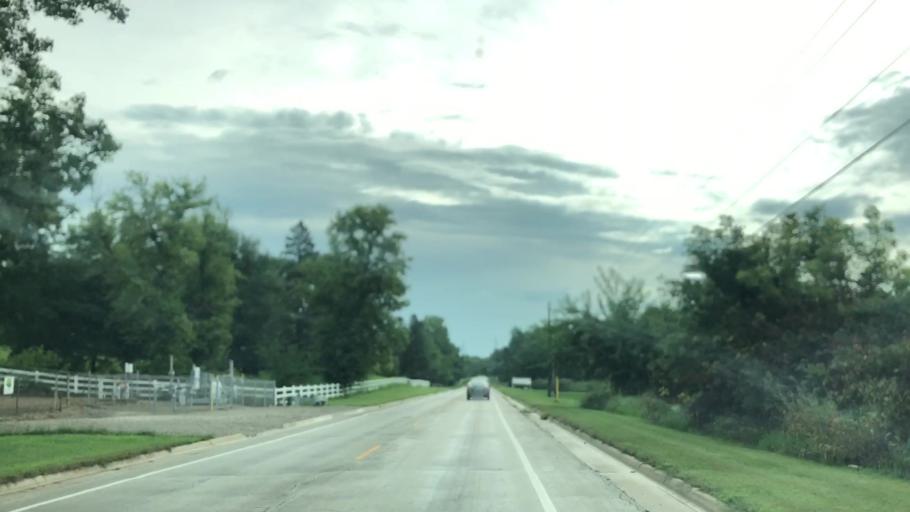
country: US
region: Iowa
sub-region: Marshall County
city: Marshalltown
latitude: 42.0490
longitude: -92.9522
